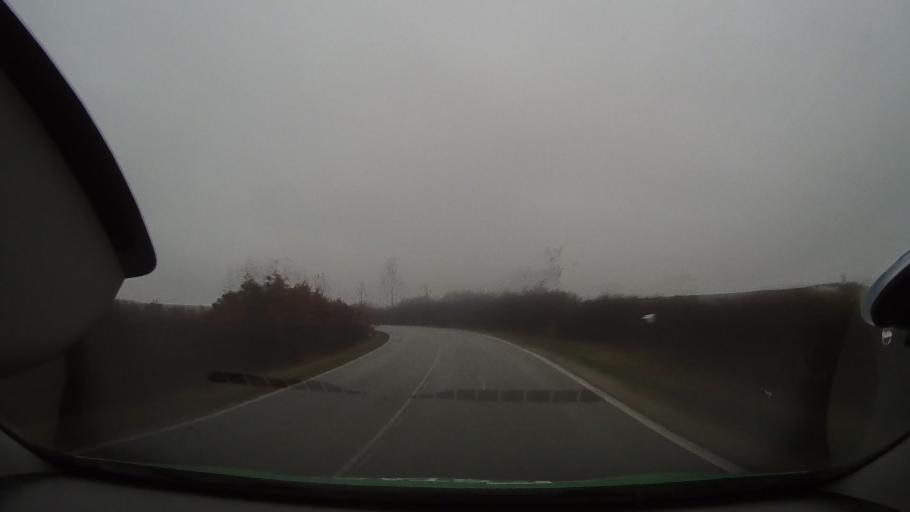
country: RO
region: Arad
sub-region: Comuna Craiova
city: Craiova
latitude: 46.6014
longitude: 21.9656
